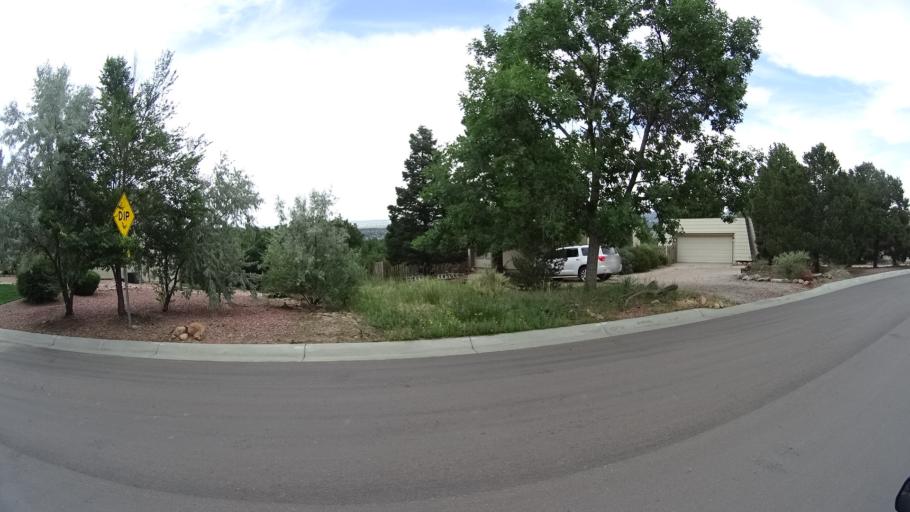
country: US
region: Colorado
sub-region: El Paso County
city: Colorado Springs
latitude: 38.9051
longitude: -104.8410
